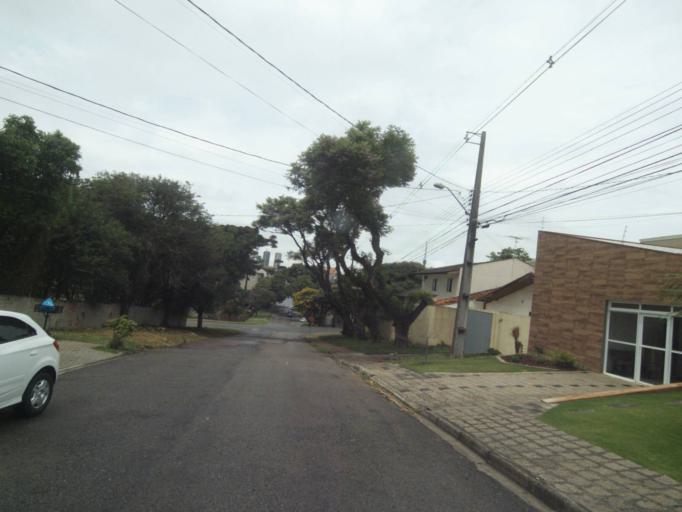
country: BR
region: Parana
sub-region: Curitiba
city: Curitiba
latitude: -25.4116
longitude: -49.2837
